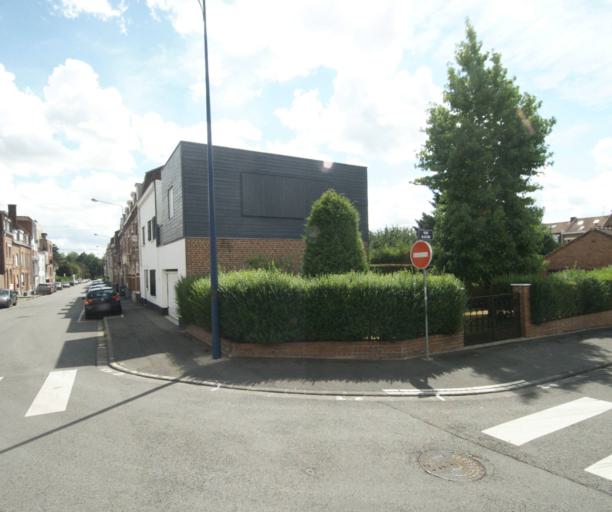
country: FR
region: Nord-Pas-de-Calais
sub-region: Departement du Nord
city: Croix
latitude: 50.6747
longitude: 3.1529
